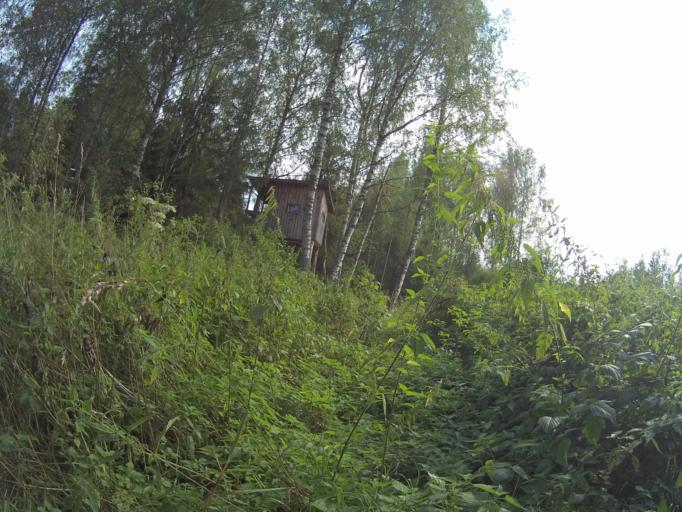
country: RU
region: Vladimir
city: Orgtrud
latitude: 56.0454
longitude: 40.6249
